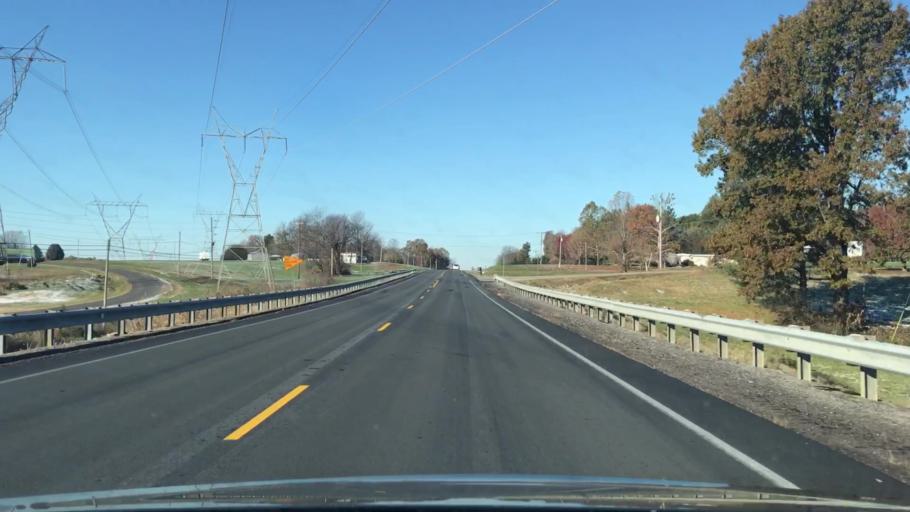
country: US
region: Kentucky
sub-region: Livingston County
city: Ledbetter
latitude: 37.0056
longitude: -88.4197
